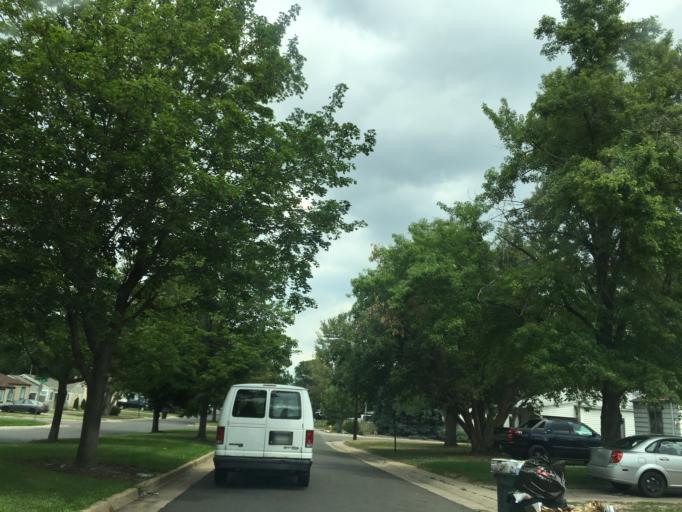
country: US
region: Colorado
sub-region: Arapahoe County
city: Sheridan
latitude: 39.6784
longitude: -105.0298
